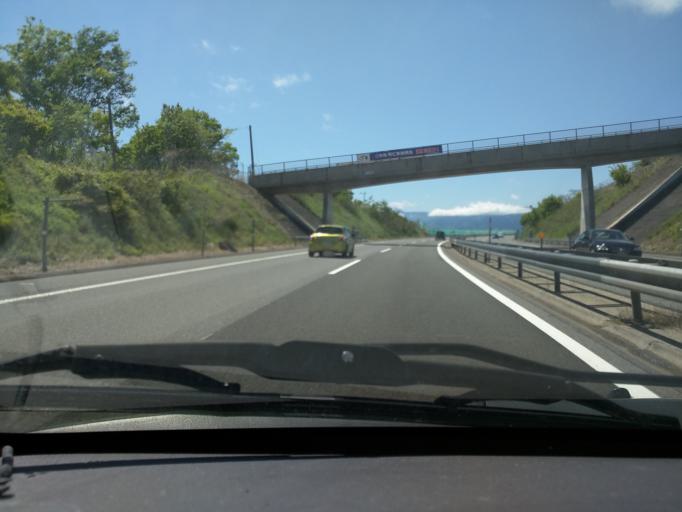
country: JP
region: Nagano
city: Nakano
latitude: 36.7750
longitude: 138.3188
